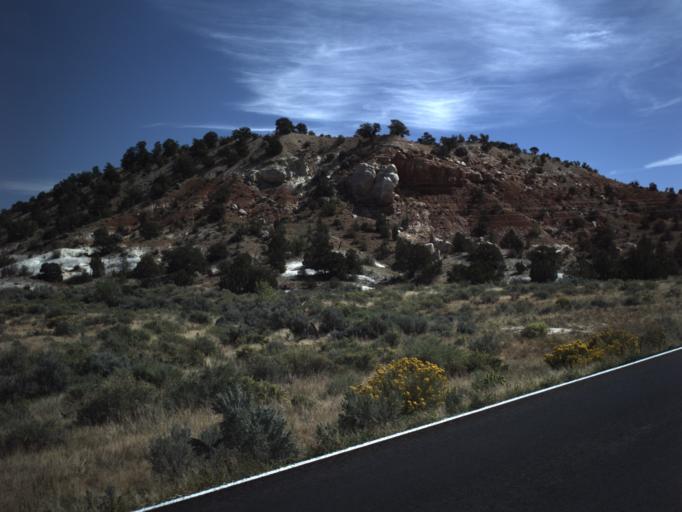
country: US
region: Utah
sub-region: Wayne County
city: Loa
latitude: 37.7762
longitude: -111.6193
